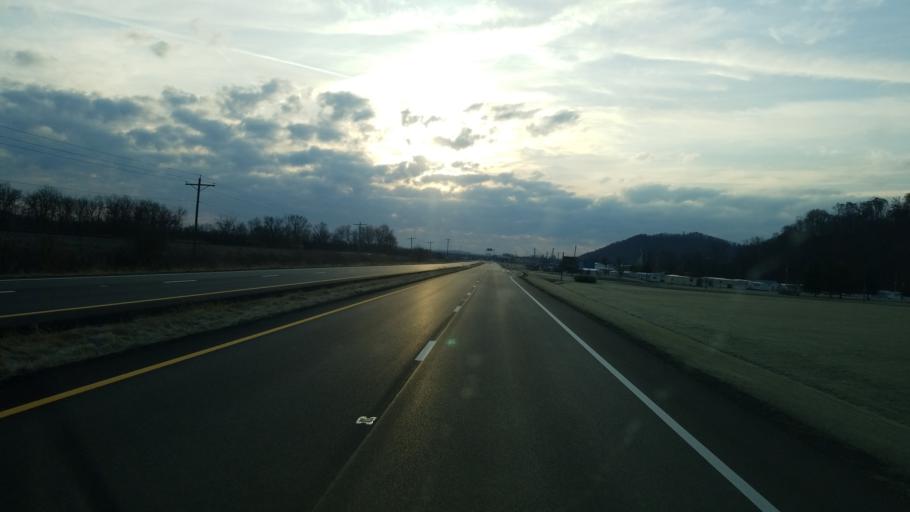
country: US
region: Ohio
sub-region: Ross County
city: Chillicothe
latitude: 39.2972
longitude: -82.9524
